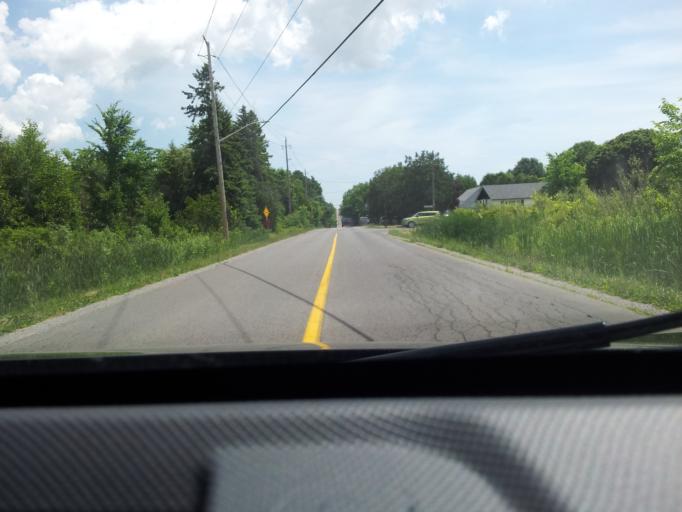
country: CA
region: Ontario
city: Norfolk County
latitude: 42.8226
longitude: -80.2942
